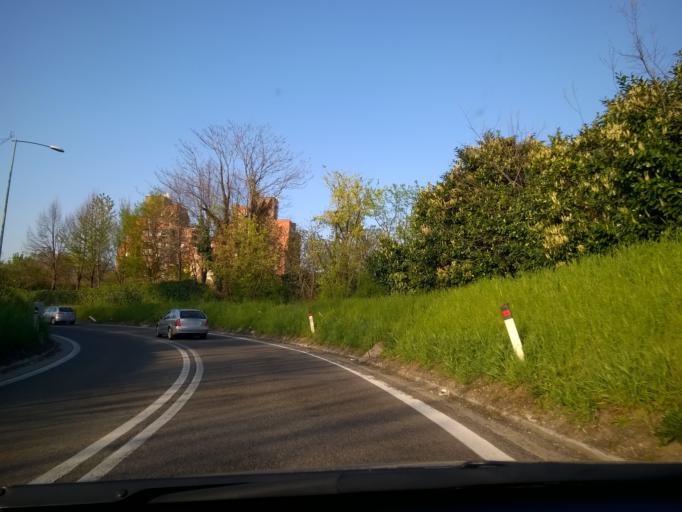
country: IT
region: Emilia-Romagna
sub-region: Provincia di Bologna
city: Quarto Inferiore
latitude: 44.5097
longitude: 11.3828
